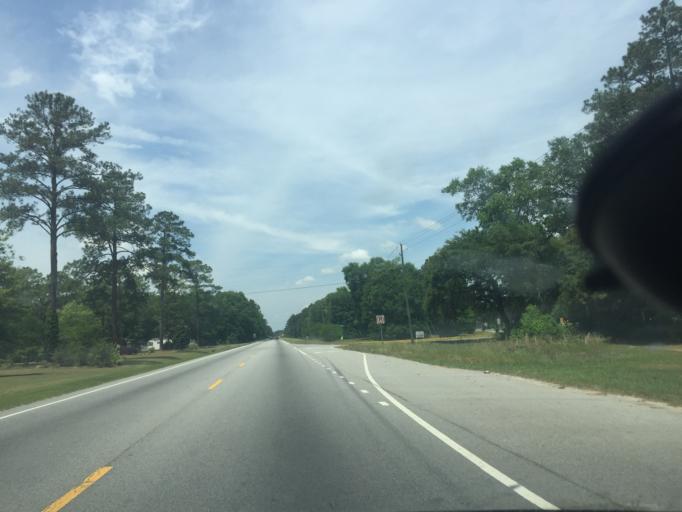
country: US
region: Georgia
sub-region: Chatham County
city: Bloomingdale
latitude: 32.1754
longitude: -81.3921
